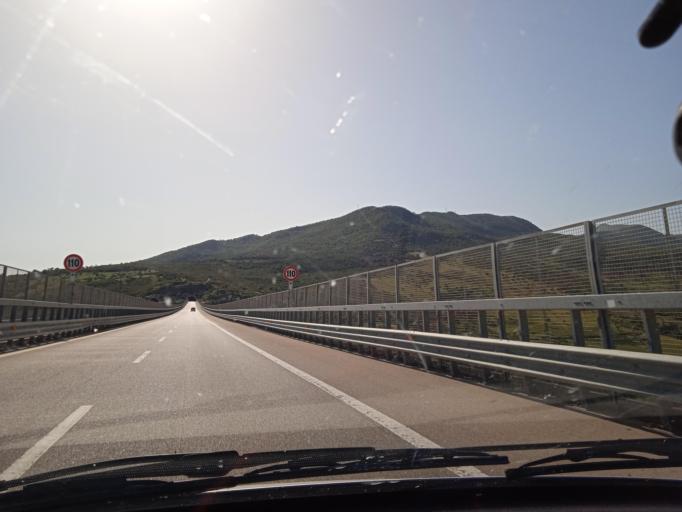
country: IT
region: Sicily
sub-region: Palermo
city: Finale
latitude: 38.0087
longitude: 14.1734
